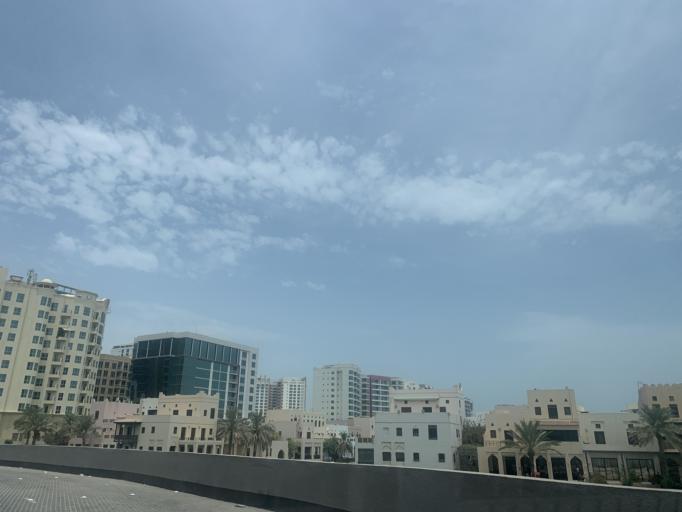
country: BH
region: Muharraq
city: Al Hadd
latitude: 26.2848
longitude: 50.6675
